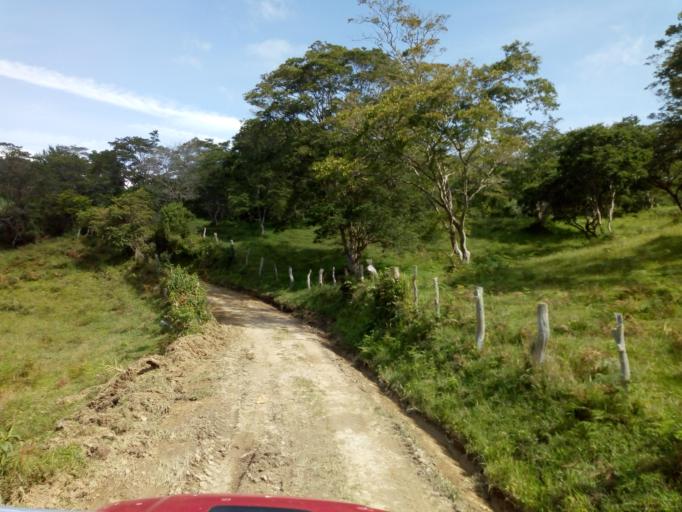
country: CO
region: Boyaca
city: Moniquira
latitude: 5.8691
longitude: -73.5035
